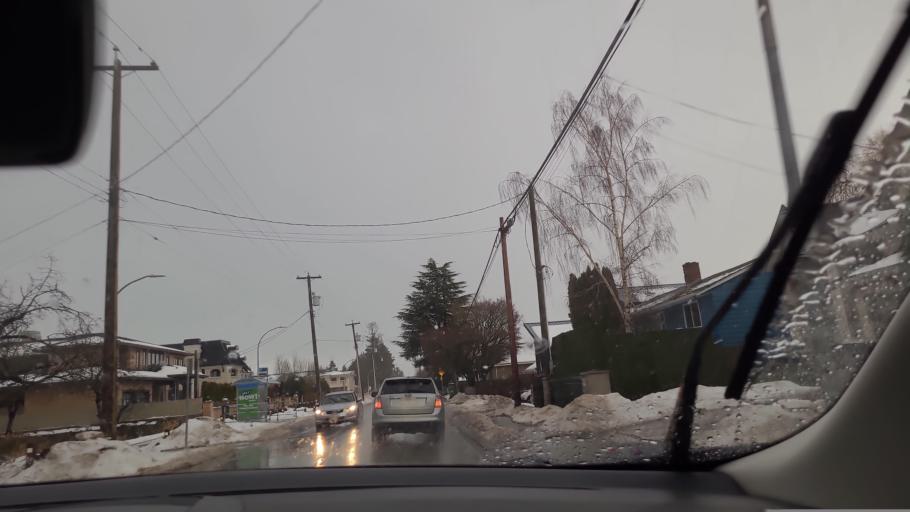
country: CA
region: British Columbia
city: Richmond
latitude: 49.1311
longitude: -123.1589
